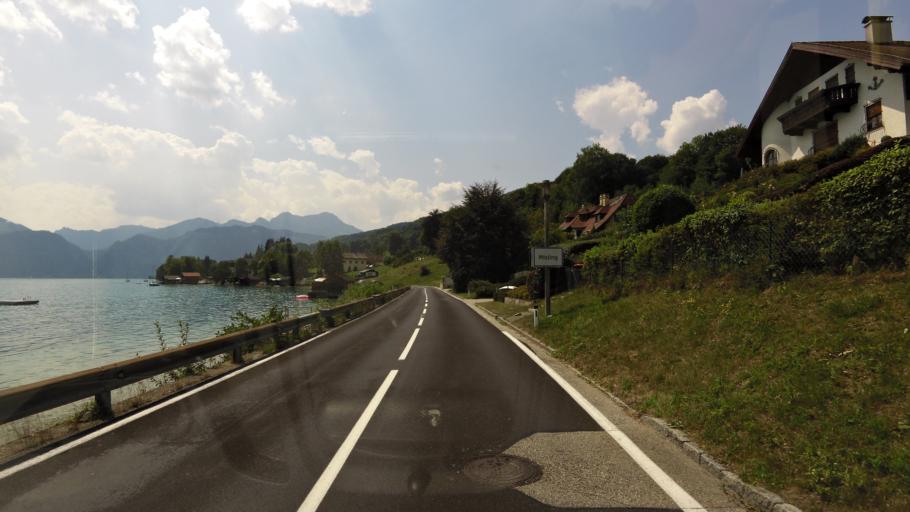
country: AT
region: Upper Austria
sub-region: Politischer Bezirk Vocklabruck
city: Steinbach am Attersee
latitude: 47.8330
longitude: 13.5217
